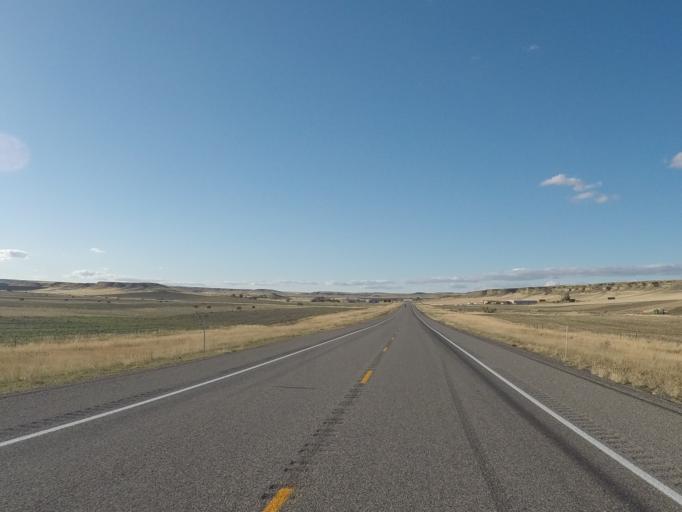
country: US
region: Montana
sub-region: Yellowstone County
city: Billings
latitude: 45.8649
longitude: -108.6569
